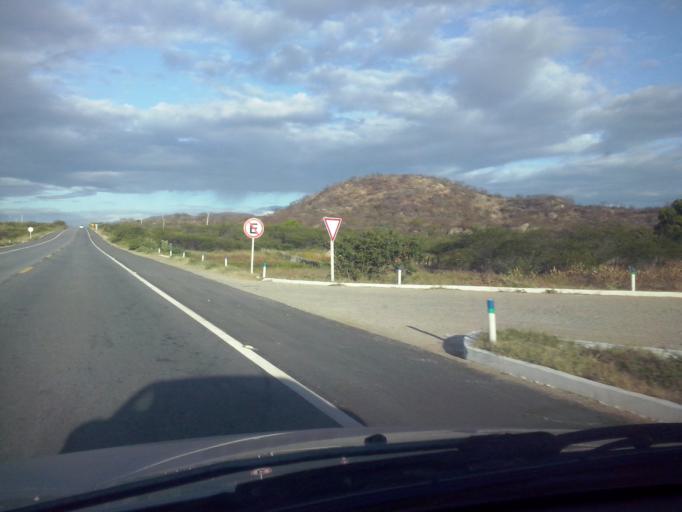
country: BR
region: Paraiba
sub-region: Patos
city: Patos
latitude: -6.9079
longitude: -37.5072
